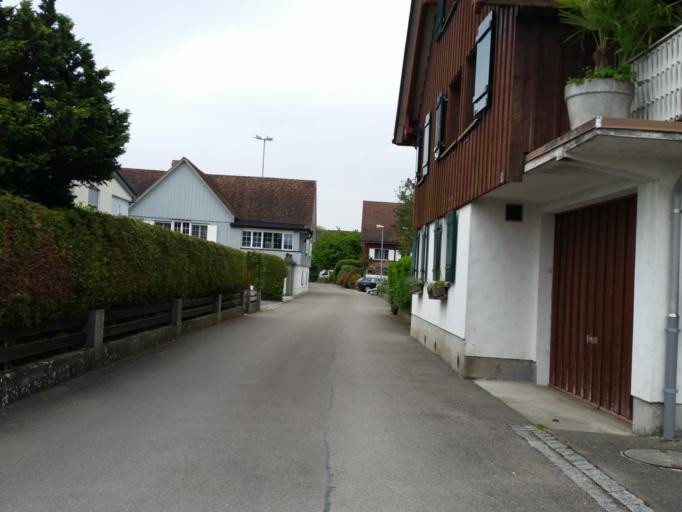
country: CH
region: Thurgau
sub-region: Arbon District
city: Uttwil
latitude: 47.5973
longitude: 9.3193
